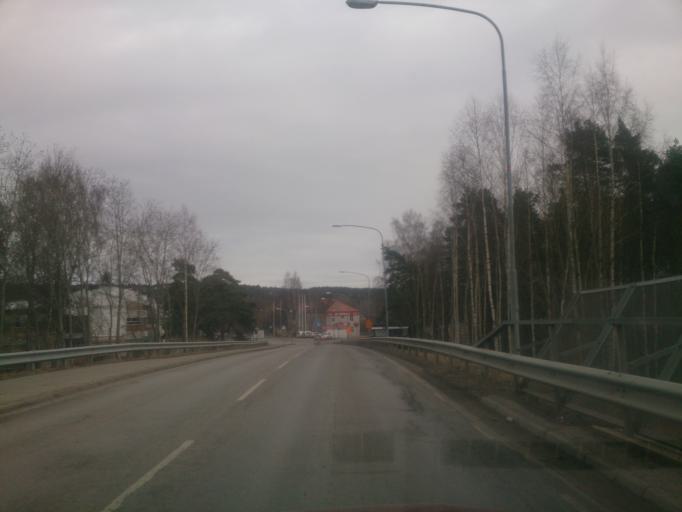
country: SE
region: OEstergoetland
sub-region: Norrkopings Kommun
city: Jursla
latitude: 58.6620
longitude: 16.1781
